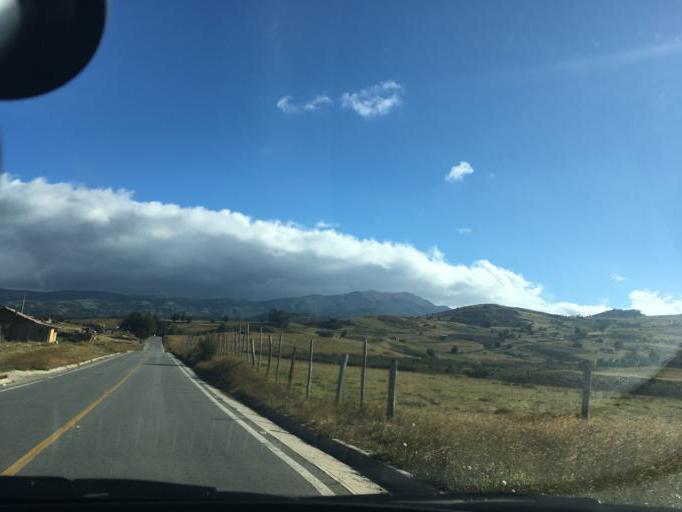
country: CO
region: Boyaca
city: Pesca
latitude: 5.5283
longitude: -72.9780
